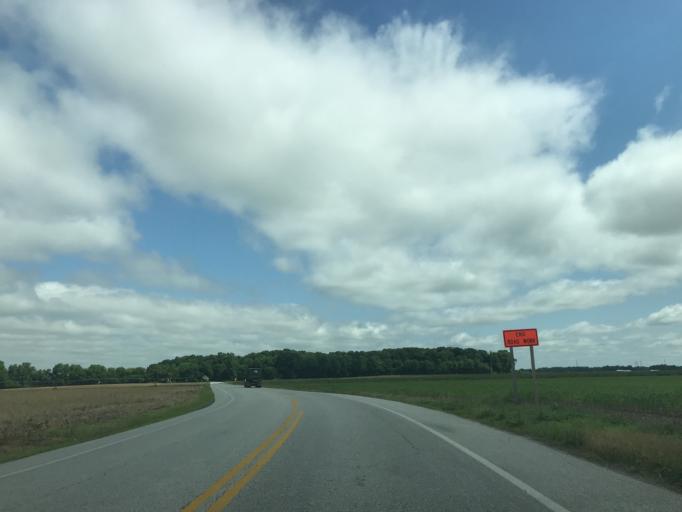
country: US
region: Maryland
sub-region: Caroline County
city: Ridgely
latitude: 38.9162
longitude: -75.8937
